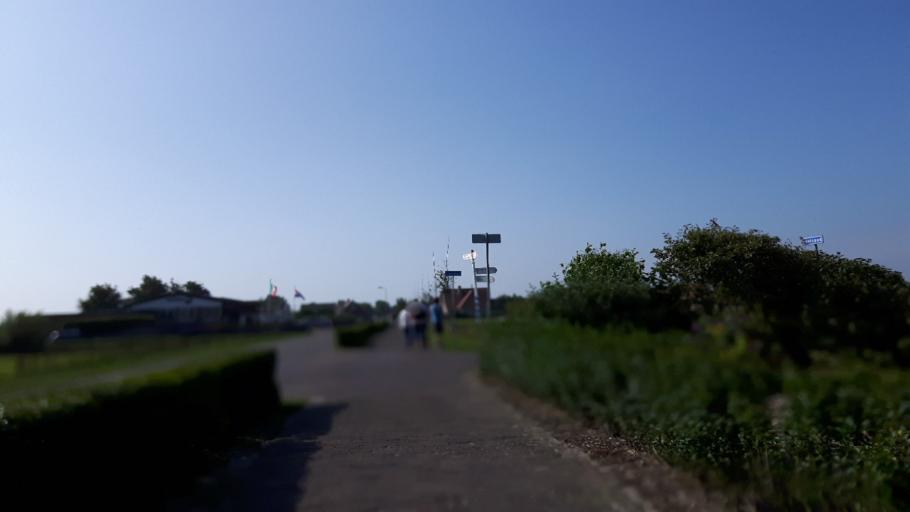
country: NL
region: Friesland
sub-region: Gemeente Ameland
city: Nes
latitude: 53.4528
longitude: 5.8021
